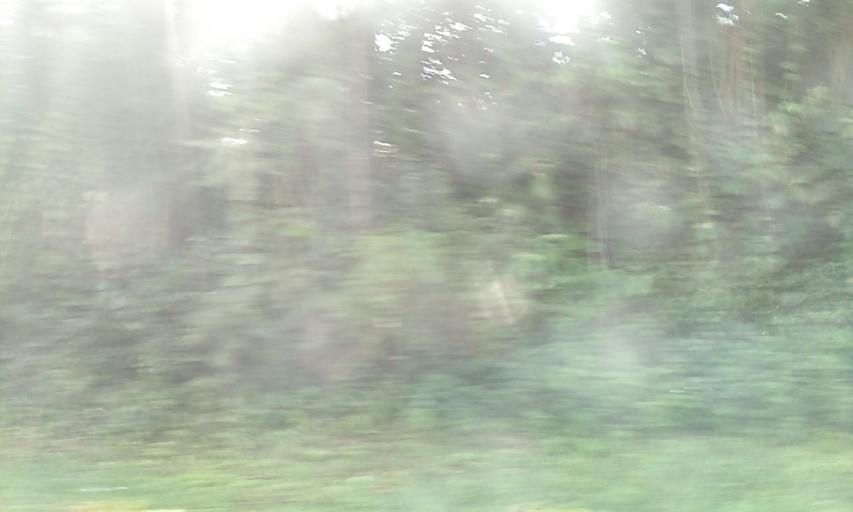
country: UG
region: Central Region
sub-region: Kampala District
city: Kampala
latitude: 0.3367
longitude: 32.5977
